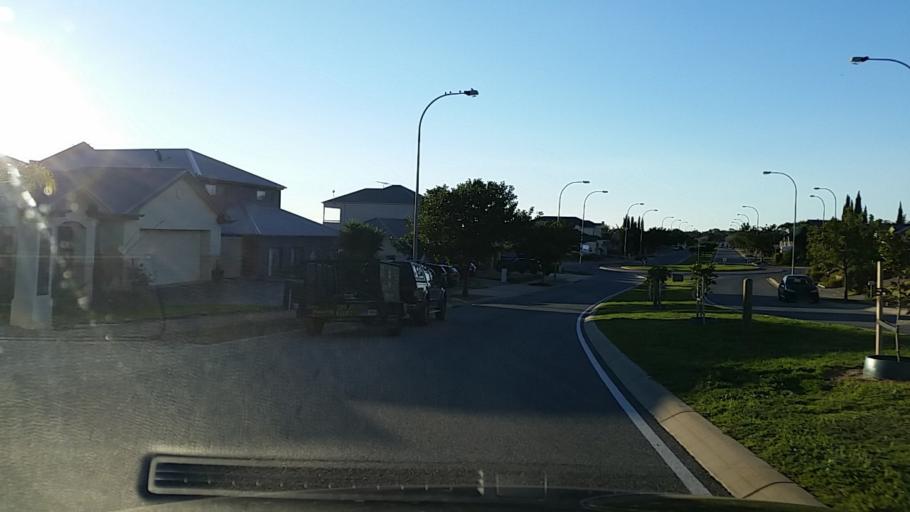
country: AU
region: South Australia
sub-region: Onkaparinga
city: Moana
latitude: -35.2088
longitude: 138.4836
